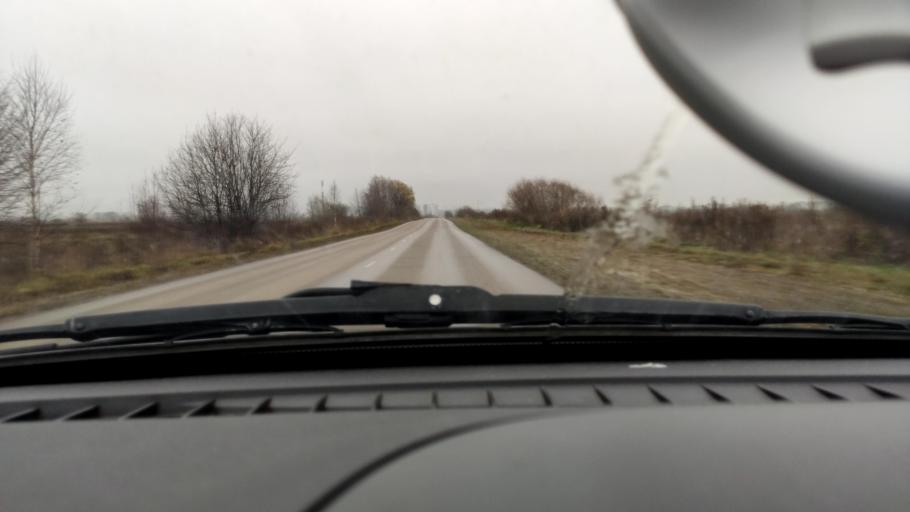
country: RU
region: Perm
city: Kondratovo
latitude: 57.9995
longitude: 56.0746
